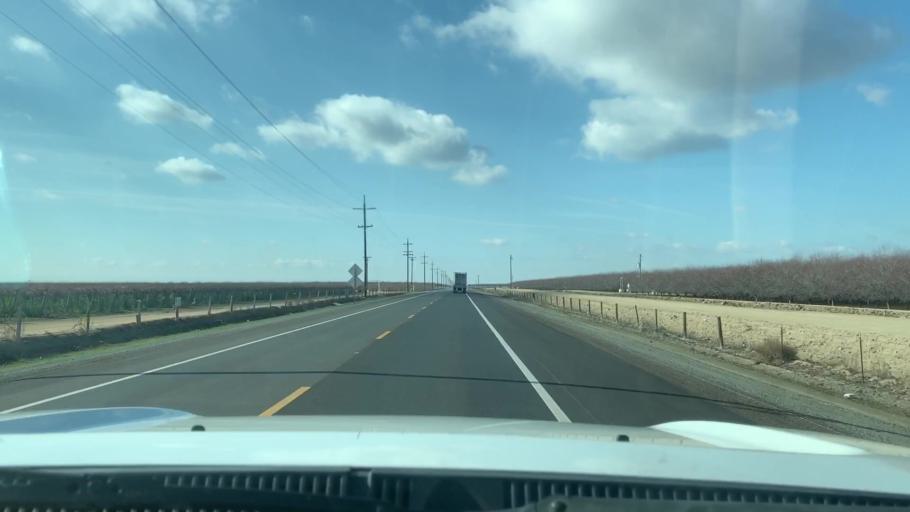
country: US
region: California
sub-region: Kern County
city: McFarland
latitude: 35.6020
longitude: -119.2303
